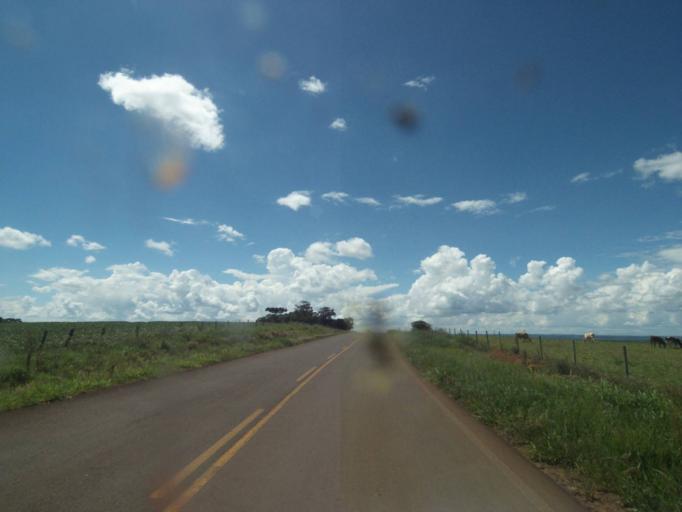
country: BR
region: Parana
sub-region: Pinhao
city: Pinhao
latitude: -25.8056
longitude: -52.0725
